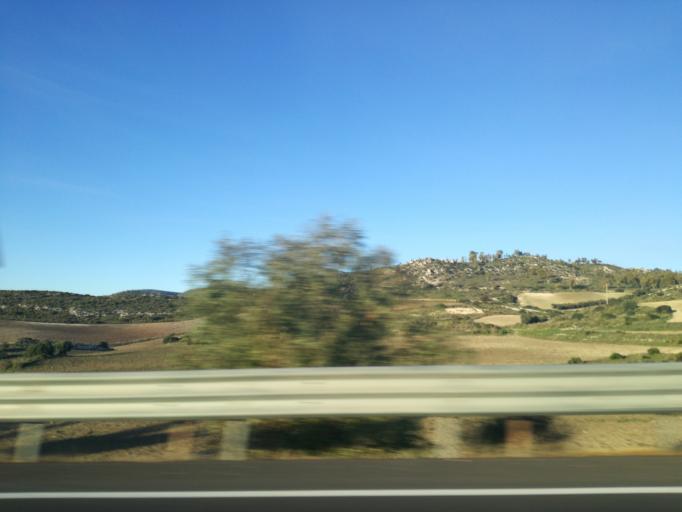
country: IT
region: Sicily
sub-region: Catania
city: San Michele di Ganzaria
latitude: 37.2160
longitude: 14.4164
